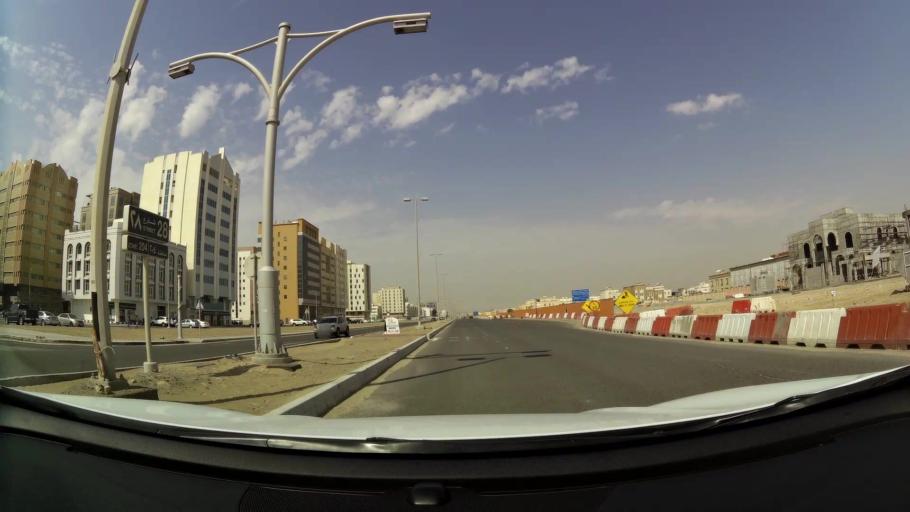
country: AE
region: Abu Dhabi
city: Abu Dhabi
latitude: 24.3180
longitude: 54.5395
